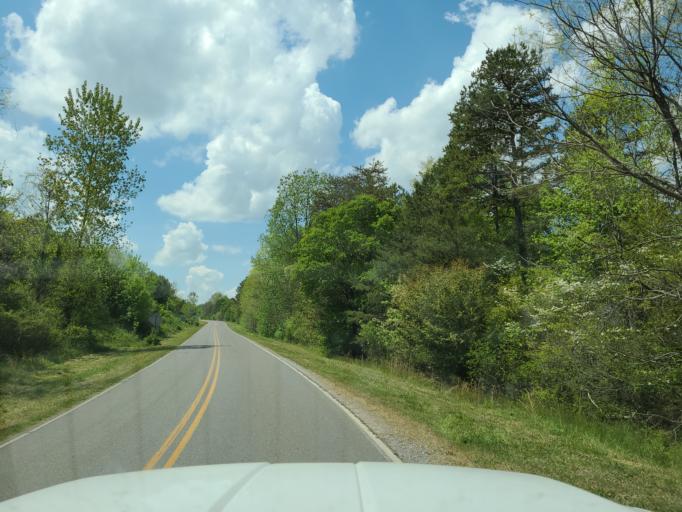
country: US
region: North Carolina
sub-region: Cleveland County
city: Shelby
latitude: 35.3281
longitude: -81.4772
